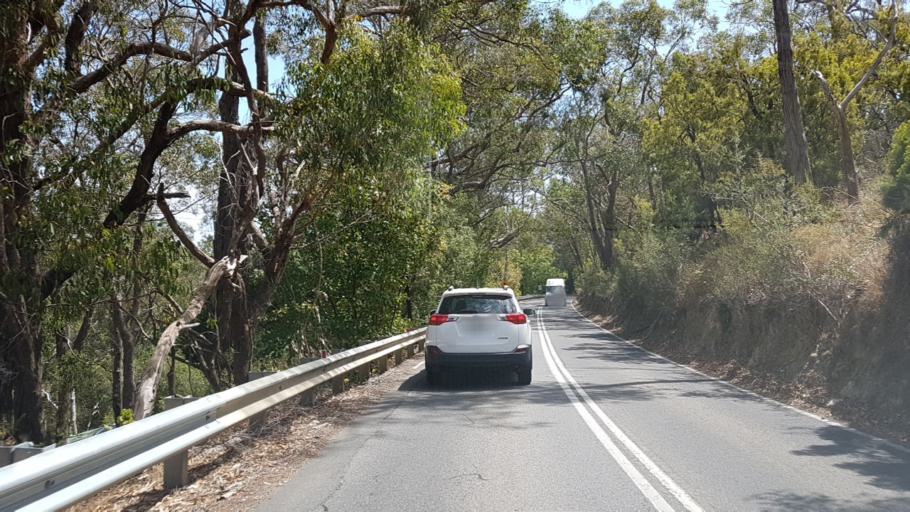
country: AU
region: South Australia
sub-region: Adelaide Hills
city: Upper Sturt
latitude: -35.0163
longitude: 138.6918
